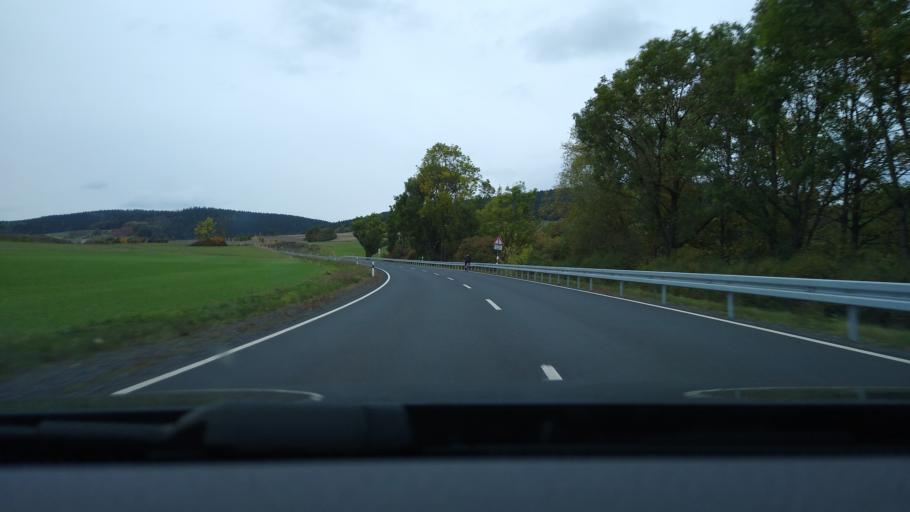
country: DE
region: Thuringia
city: Eisfeld
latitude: 50.4505
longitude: 10.9350
